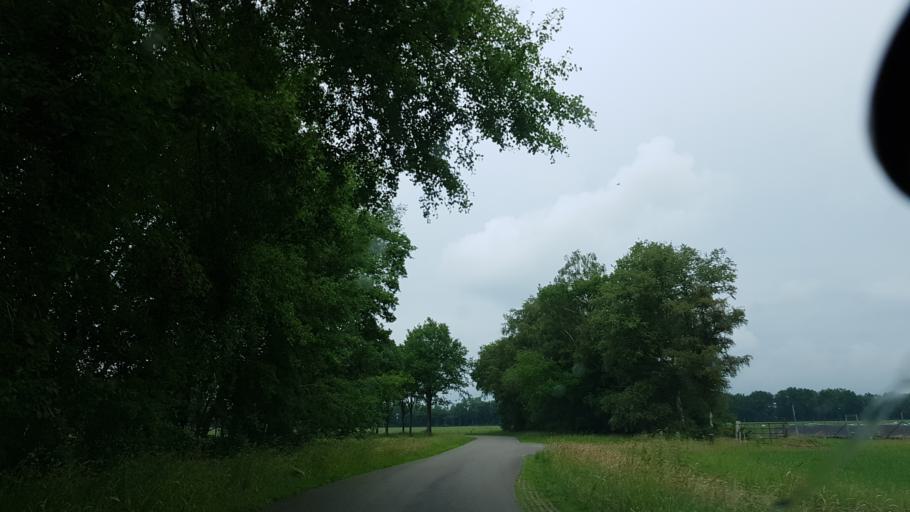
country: NL
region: Drenthe
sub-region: Gemeente Tynaarlo
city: Tynaarlo
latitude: 53.0278
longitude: 6.6044
